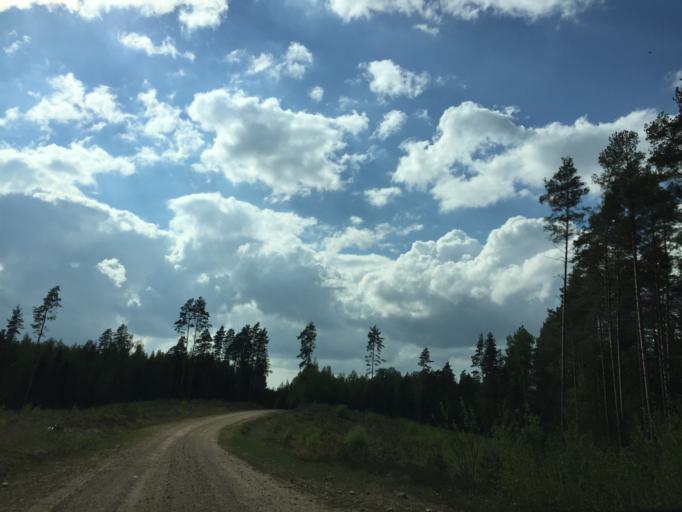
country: LV
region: Sigulda
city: Sigulda
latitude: 57.2956
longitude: 24.8380
